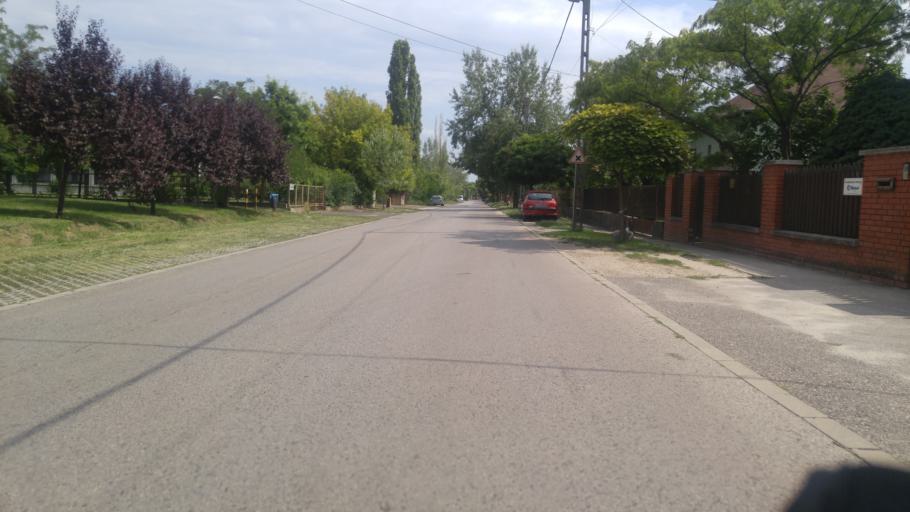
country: HU
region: Budapest
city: Budapest XVII. keruelet
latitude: 47.4760
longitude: 19.2488
